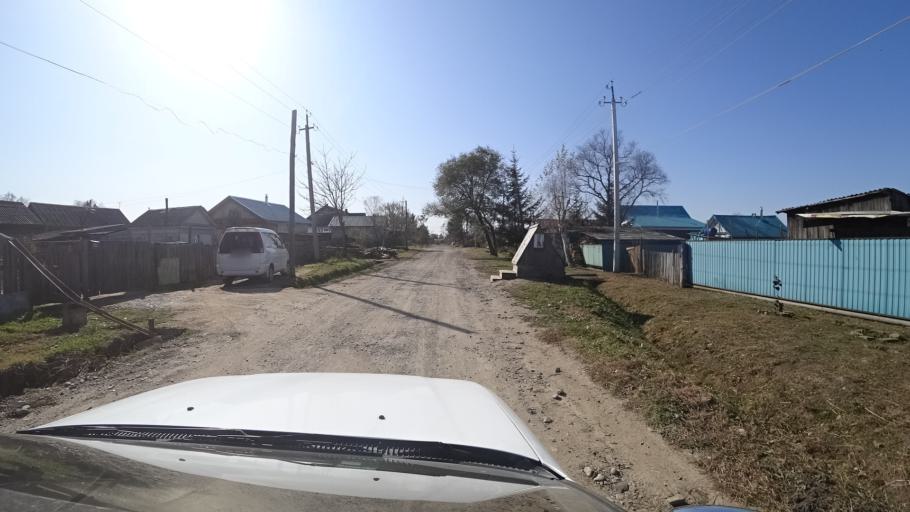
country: RU
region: Primorskiy
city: Dal'nerechensk
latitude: 45.9319
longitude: 133.7537
